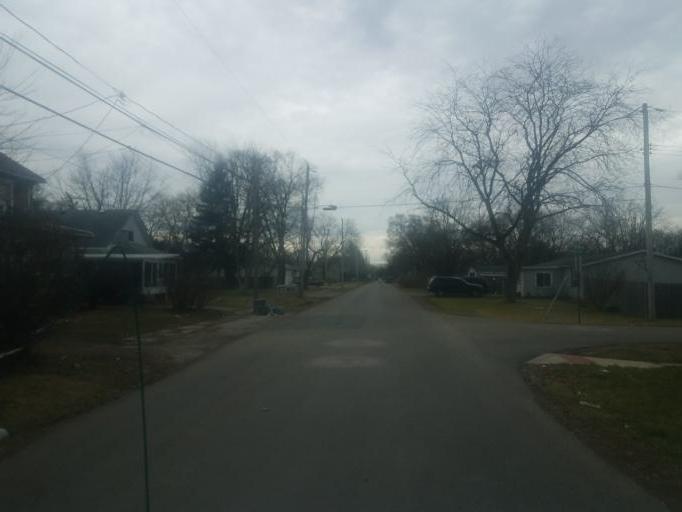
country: US
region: Ohio
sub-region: Marion County
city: Marion
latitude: 40.5983
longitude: -83.1198
